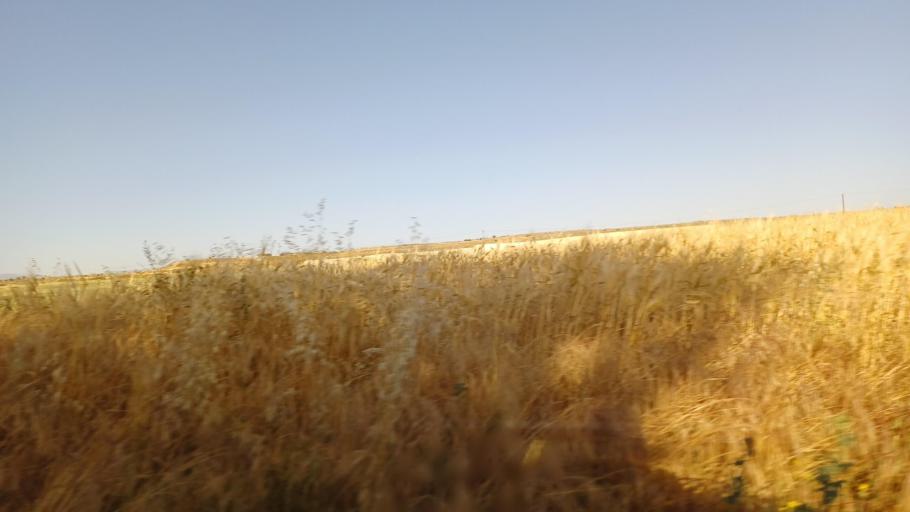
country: CY
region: Lefkosia
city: Mammari
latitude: 35.1600
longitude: 33.2474
